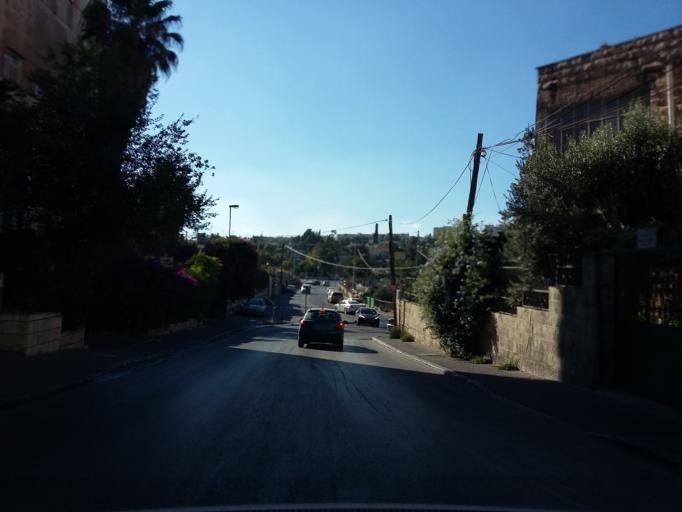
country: PS
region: West Bank
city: East Jerusalem
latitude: 31.7905
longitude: 35.2304
